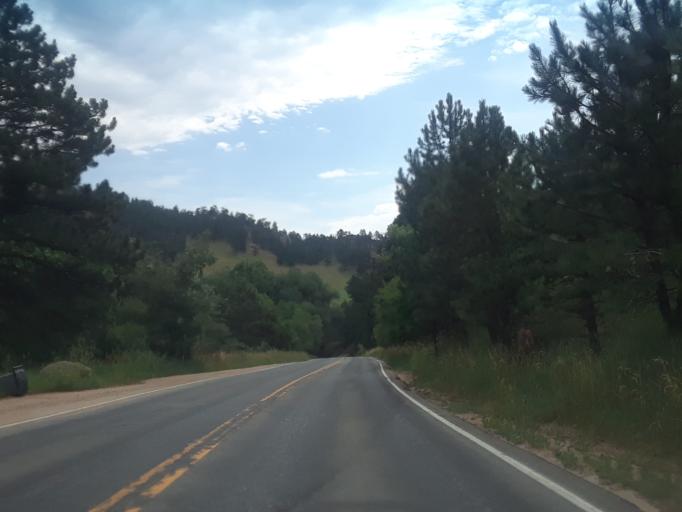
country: US
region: Colorado
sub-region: Boulder County
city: Boulder
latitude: 40.0252
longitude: -105.3063
